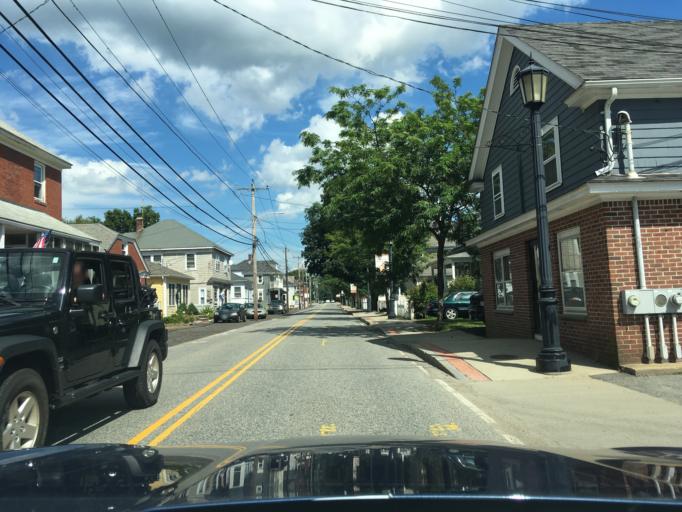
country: US
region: Rhode Island
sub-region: Bristol County
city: Barrington
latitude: 41.7393
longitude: -71.3122
